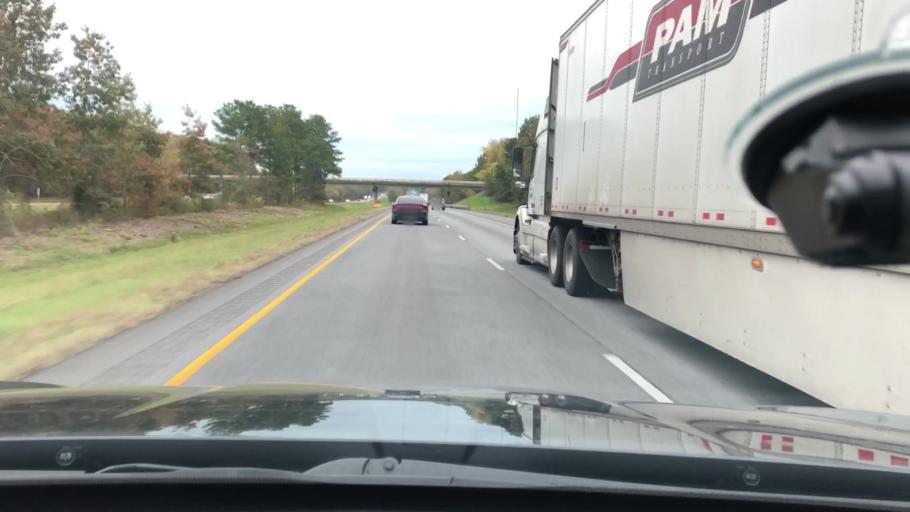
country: US
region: Arkansas
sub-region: Hempstead County
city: Hope
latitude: 33.6232
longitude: -93.7694
